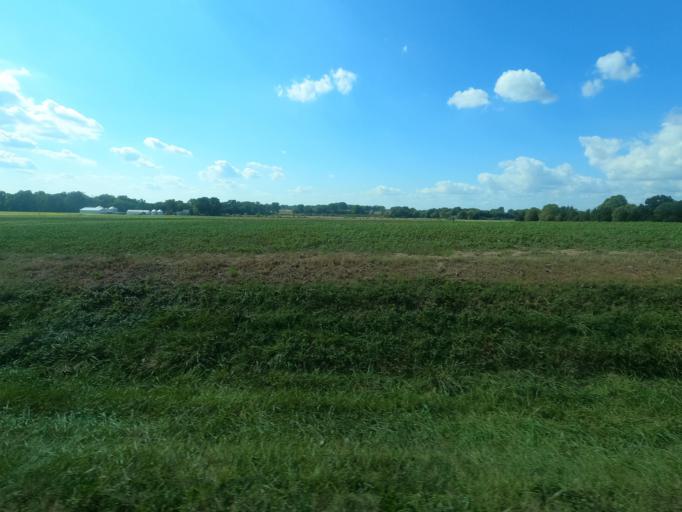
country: US
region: Illinois
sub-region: Massac County
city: Metropolis
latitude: 37.2189
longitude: -88.7292
